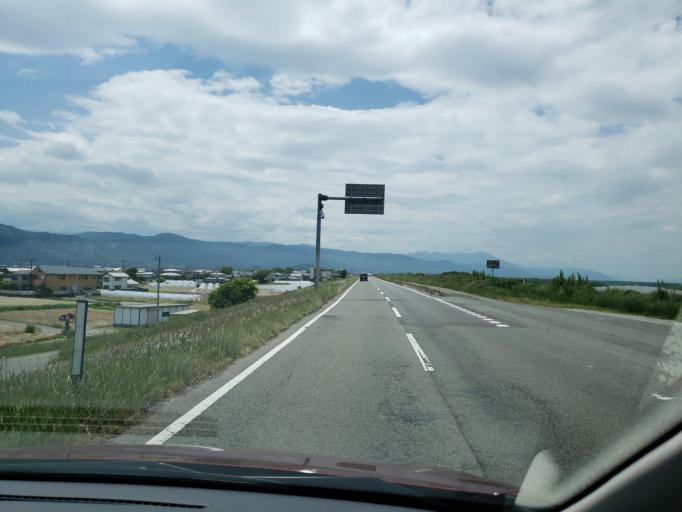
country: JP
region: Tokushima
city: Ishii
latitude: 34.0976
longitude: 134.4237
